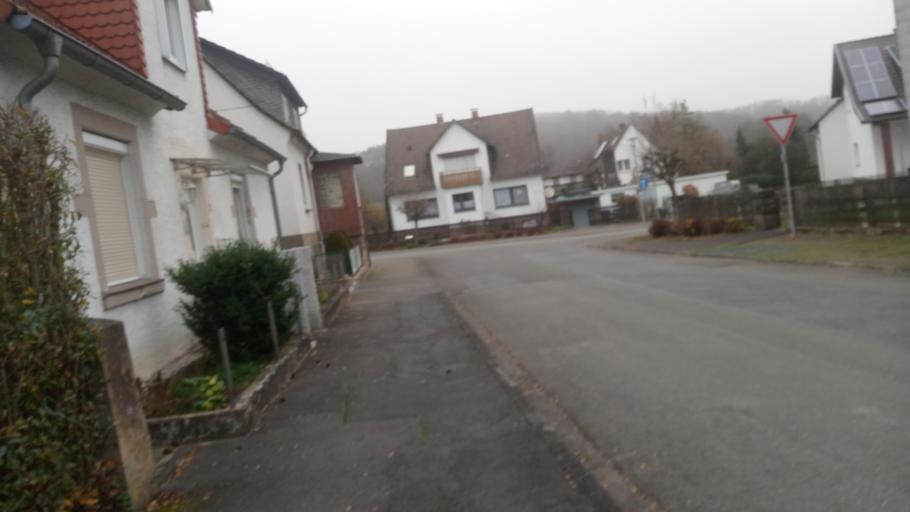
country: DE
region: North Rhine-Westphalia
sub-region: Regierungsbezirk Detmold
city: Willebadessen
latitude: 51.5097
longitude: 9.0018
